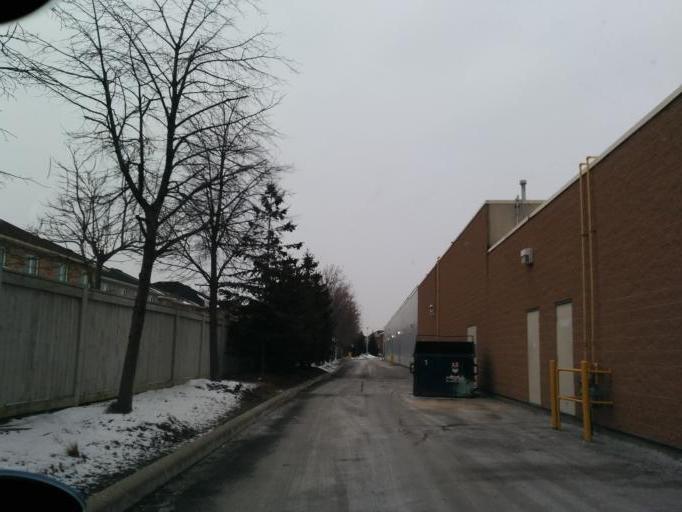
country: CA
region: Ontario
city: Brampton
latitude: 43.6362
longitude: -79.7191
